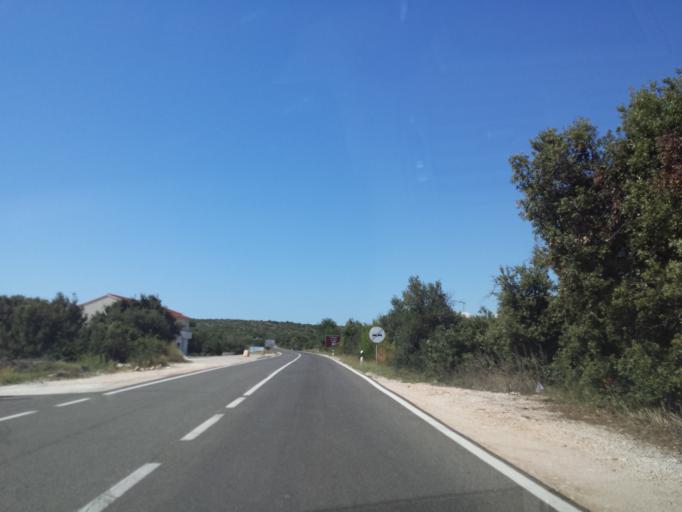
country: HR
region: Sibensko-Kniniska
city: Rogoznica
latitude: 43.5424
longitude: 15.9673
